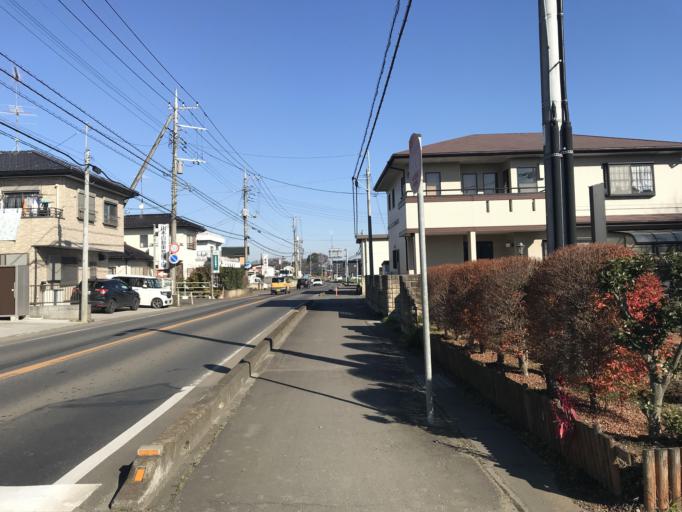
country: JP
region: Tochigi
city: Oyama
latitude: 36.2444
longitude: 139.8312
